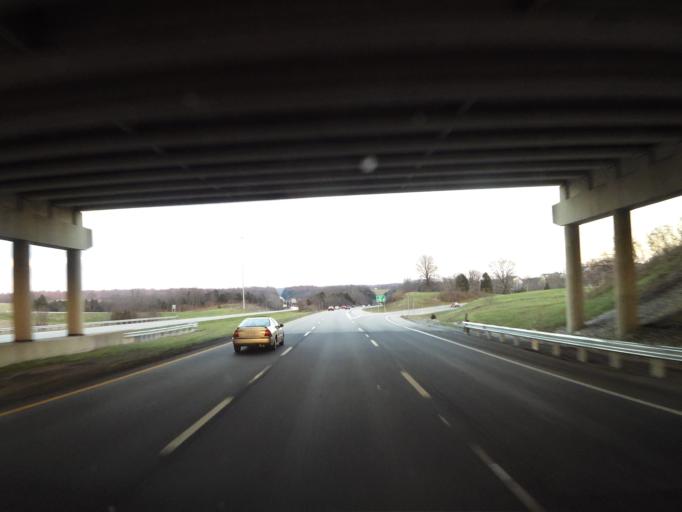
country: US
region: Kentucky
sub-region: Franklin County
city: Frankfort
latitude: 38.1582
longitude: -84.8938
